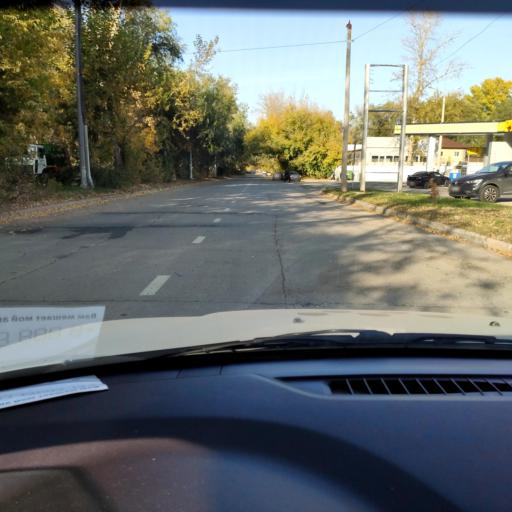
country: RU
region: Samara
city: Tol'yatti
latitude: 53.5224
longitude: 49.4310
